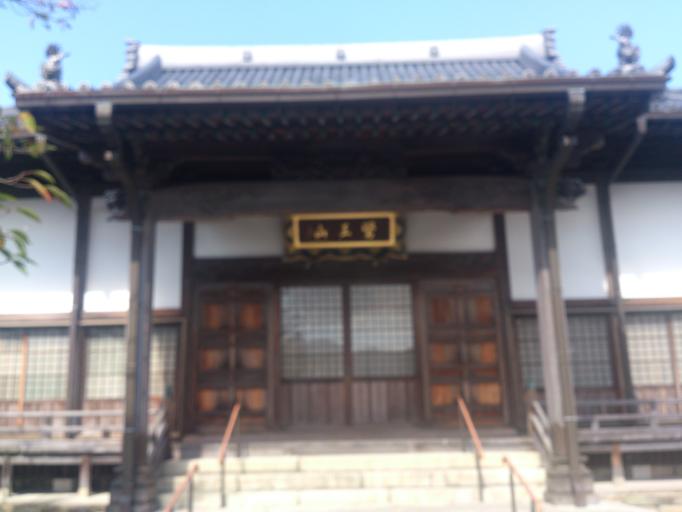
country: JP
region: Saga Prefecture
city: Imaricho-ko
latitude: 33.1862
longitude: 129.8813
